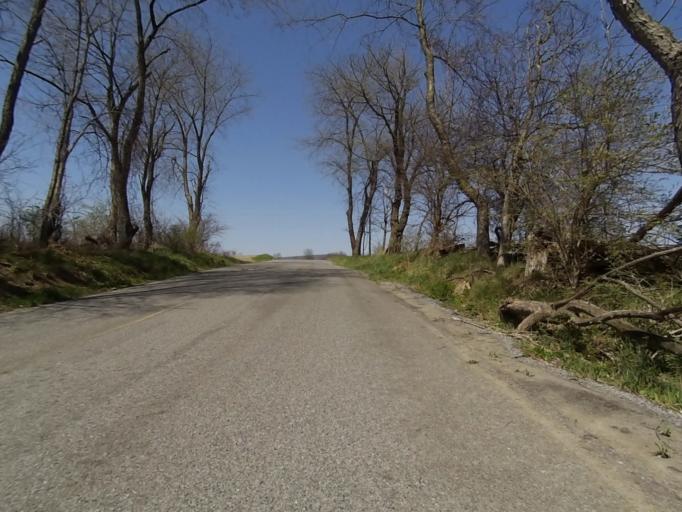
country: US
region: Pennsylvania
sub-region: Blair County
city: Williamsburg
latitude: 40.4958
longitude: -78.1775
